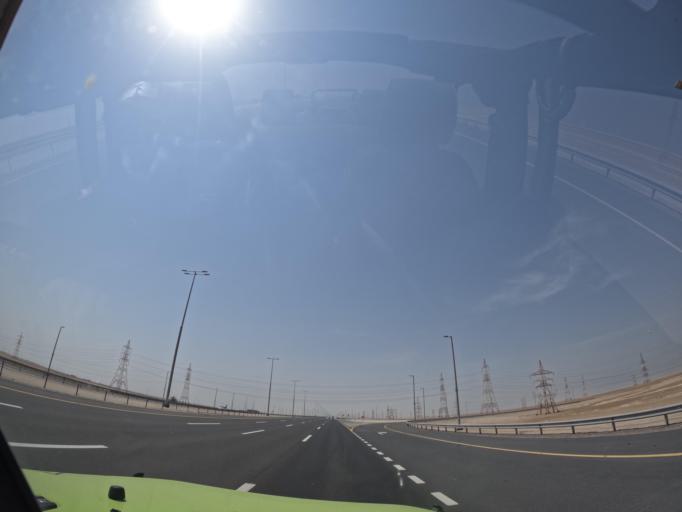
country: AE
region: Abu Dhabi
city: Abu Dhabi
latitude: 24.1561
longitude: 54.3072
